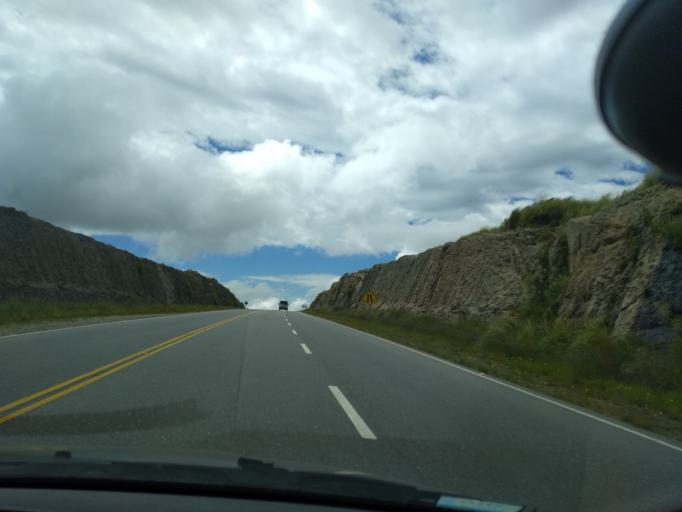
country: AR
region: Cordoba
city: Mina Clavero
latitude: -31.6102
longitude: -64.8296
